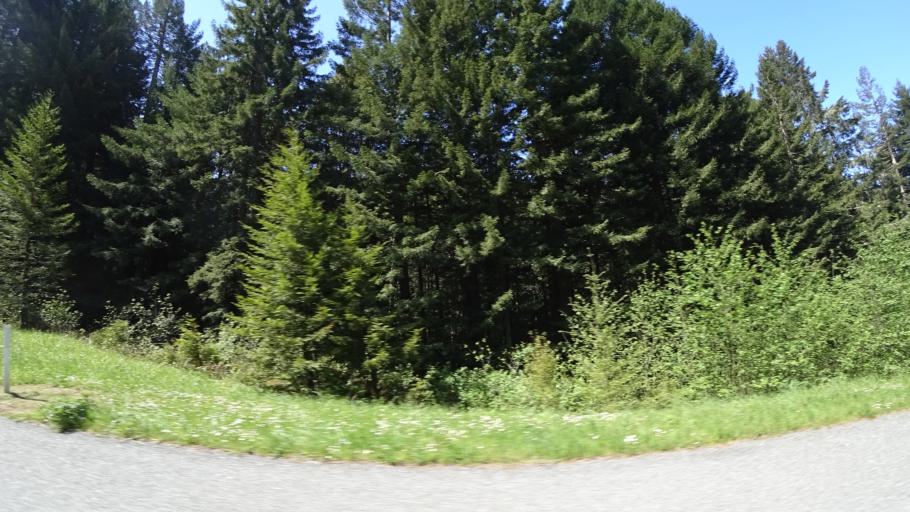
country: US
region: California
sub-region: Del Norte County
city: Bertsch-Oceanview
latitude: 41.4489
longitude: -124.0250
